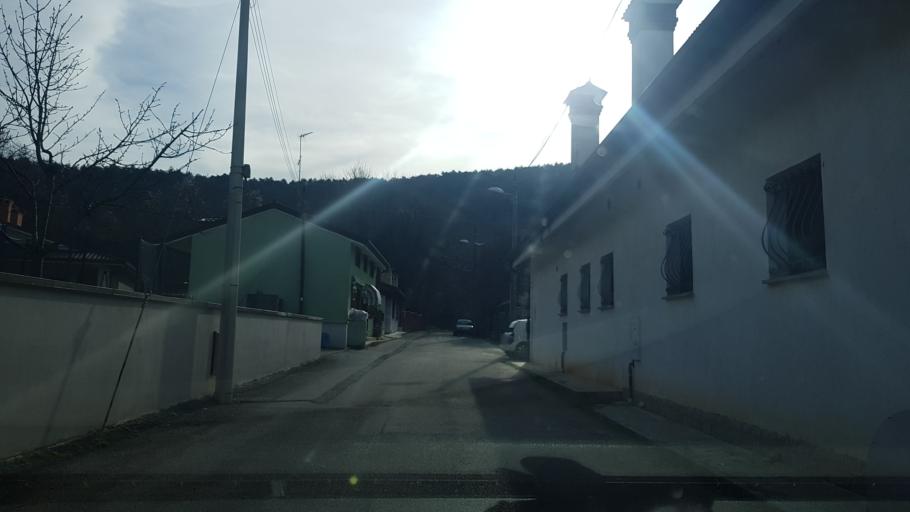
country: IT
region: Friuli Venezia Giulia
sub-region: Provincia di Gorizia
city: Gradisca d'Isonzo
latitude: 45.8840
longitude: 13.5153
